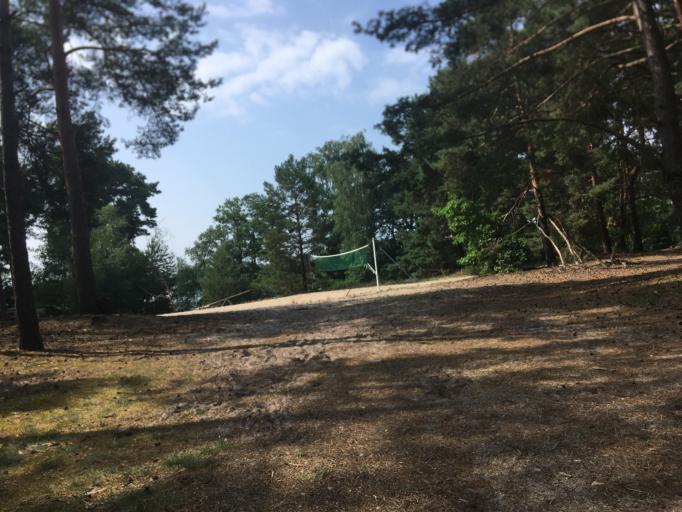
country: DE
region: Brandenburg
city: Schwerin
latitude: 52.1565
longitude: 13.6175
